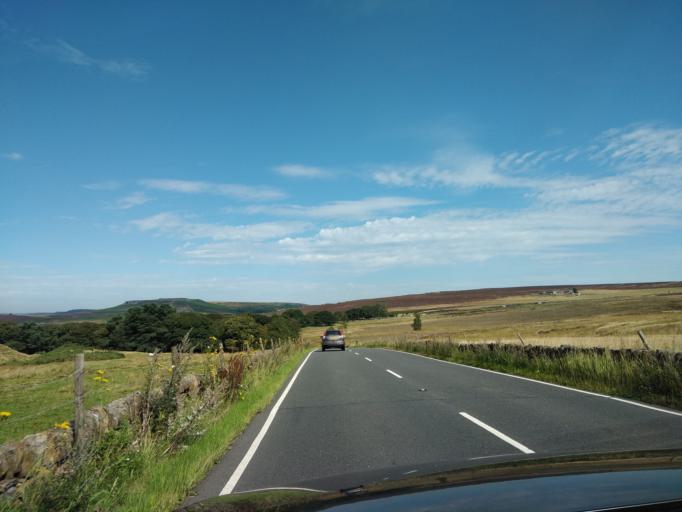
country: GB
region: England
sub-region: Derbyshire
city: Hathersage
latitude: 53.3144
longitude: -1.5991
